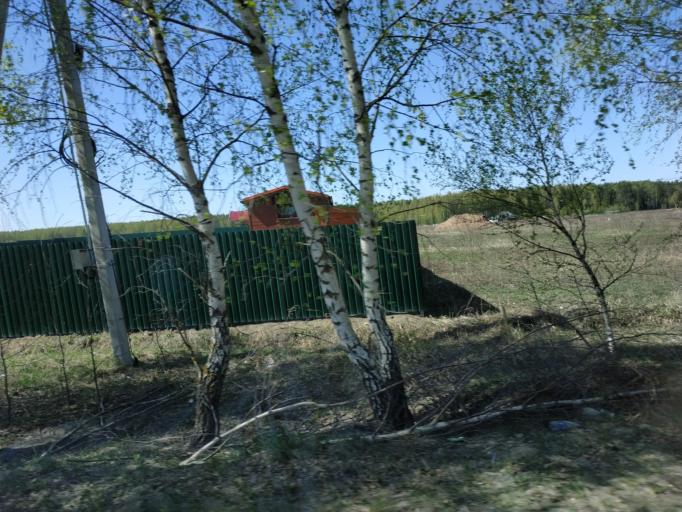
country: RU
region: Moskovskaya
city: Malyshevo
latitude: 55.4719
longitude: 38.3933
